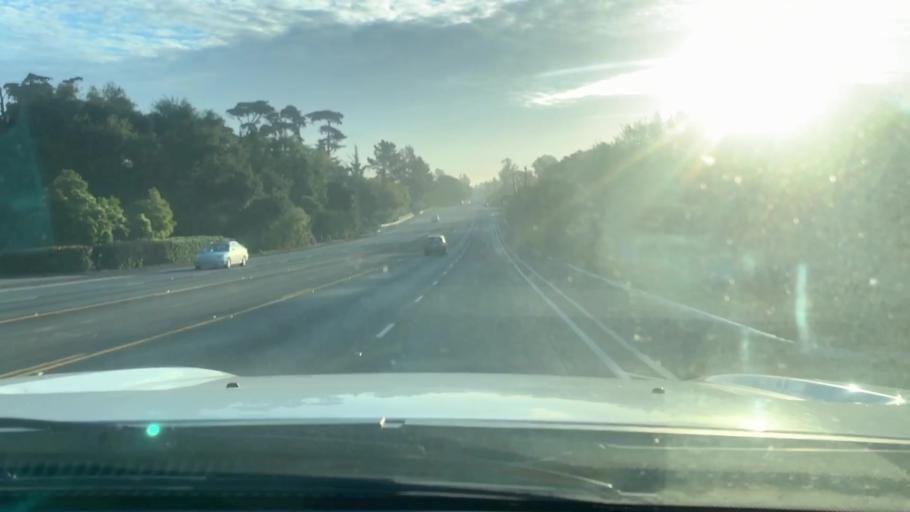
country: US
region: California
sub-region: San Luis Obispo County
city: Los Osos
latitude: 35.3065
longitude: -120.8136
